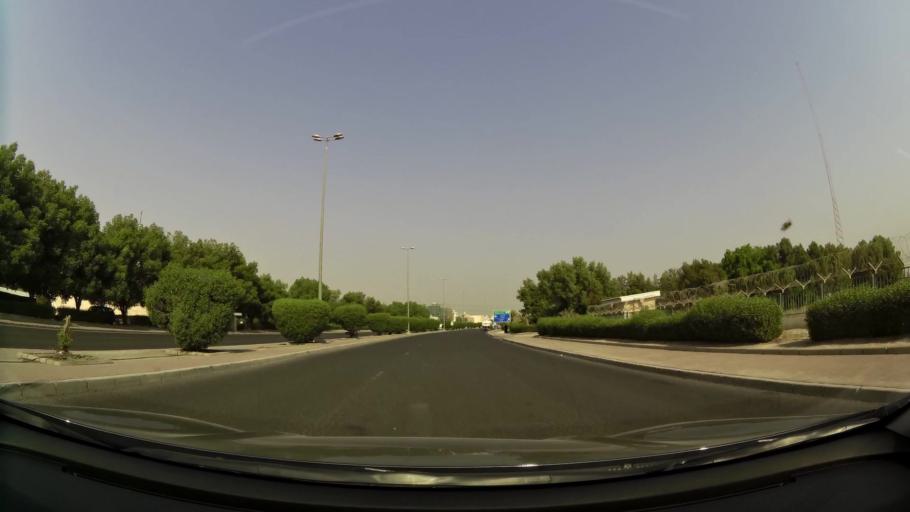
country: KW
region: Al Asimah
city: Ar Rabiyah
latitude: 29.2892
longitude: 47.8800
